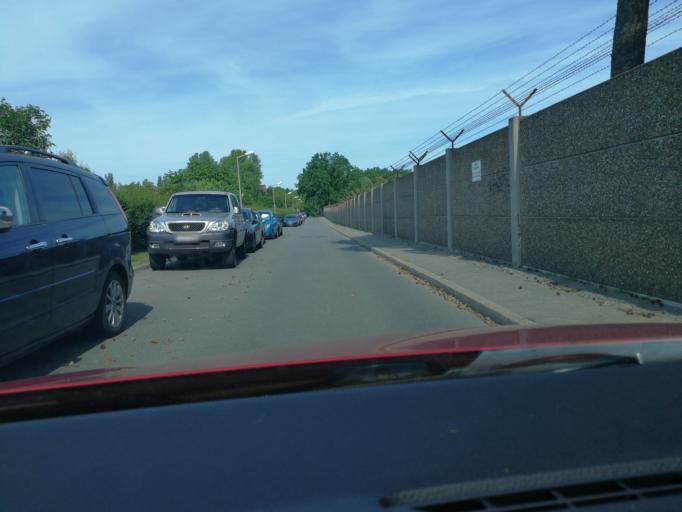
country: DE
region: Berlin
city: Reinickendorf
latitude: 52.5512
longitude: 13.3178
